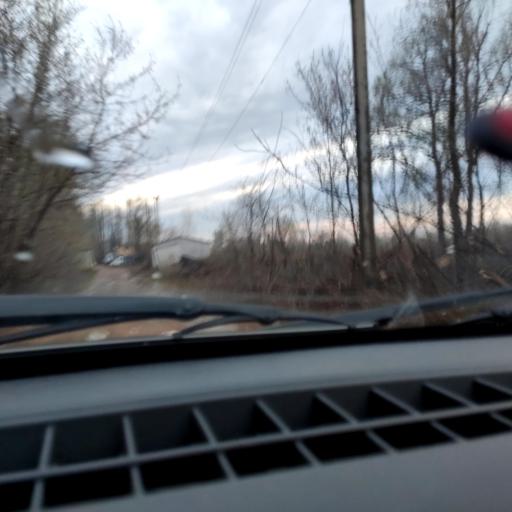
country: RU
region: Bashkortostan
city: Ufa
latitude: 54.6761
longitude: 55.9507
